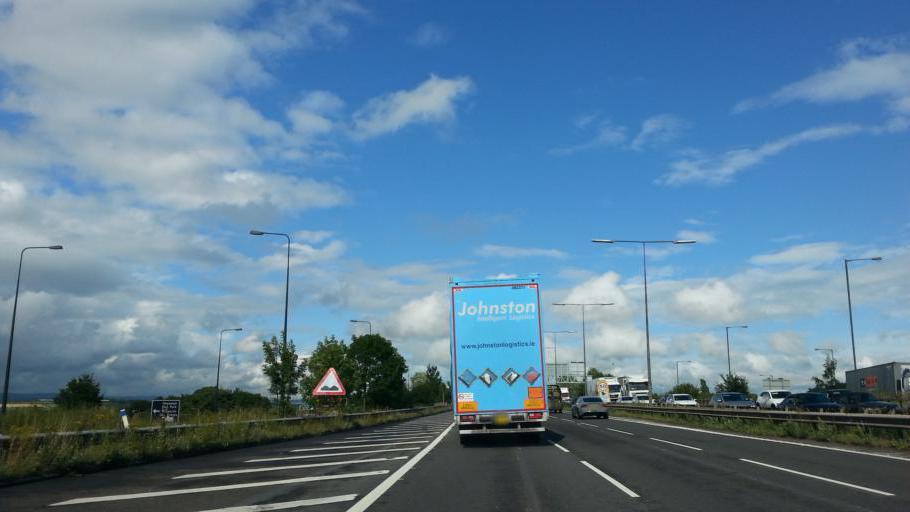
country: GB
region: England
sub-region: Borough of Bury
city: Prestwich
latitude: 53.5482
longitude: -2.2652
